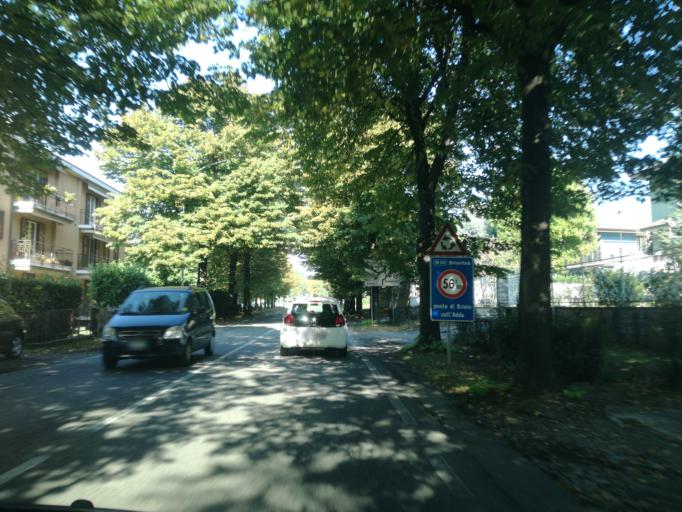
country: IT
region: Lombardy
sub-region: Provincia di Lecco
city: Robbiate
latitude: 45.6896
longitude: 9.4354
